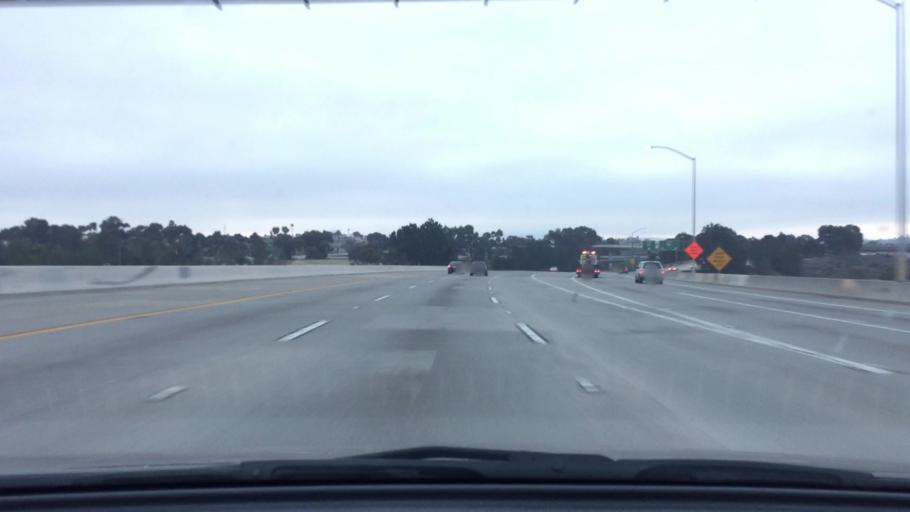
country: US
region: California
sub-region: San Diego County
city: Chula Vista
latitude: 32.6577
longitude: -117.0818
